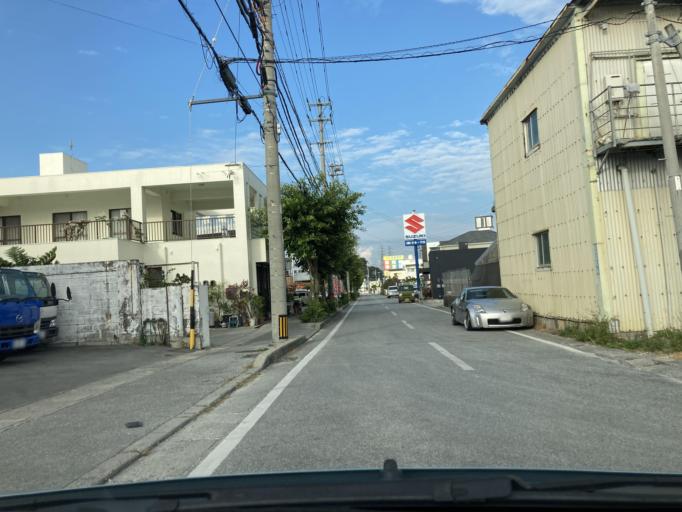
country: JP
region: Okinawa
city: Okinawa
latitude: 26.3570
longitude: 127.8073
